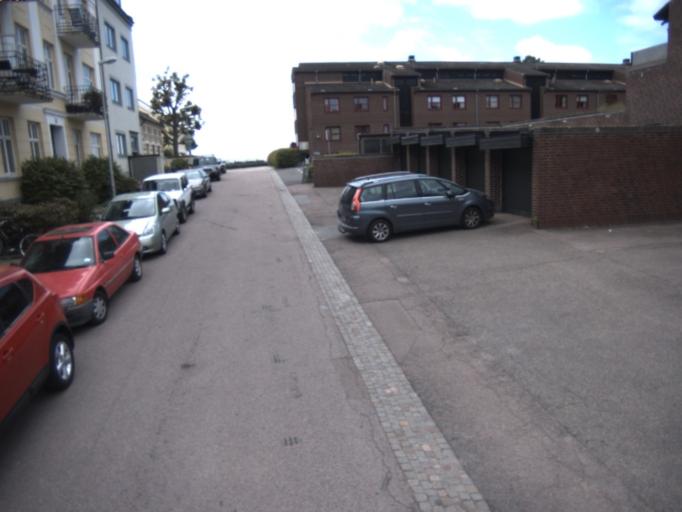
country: SE
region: Skane
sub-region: Helsingborg
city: Helsingborg
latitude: 56.0498
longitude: 12.6951
